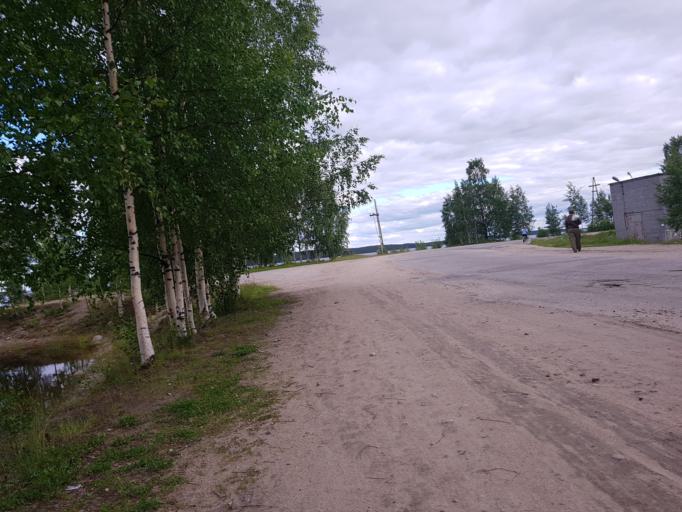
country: RU
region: Republic of Karelia
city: Kalevala
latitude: 65.1958
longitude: 31.1832
